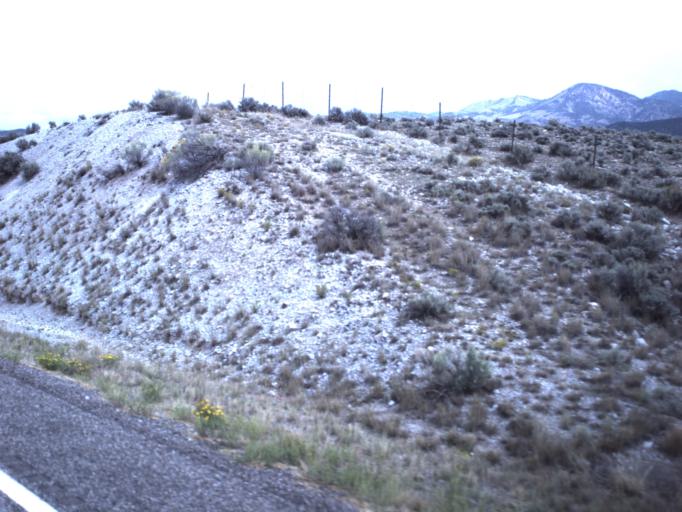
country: US
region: Utah
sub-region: Garfield County
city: Panguitch
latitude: 38.0104
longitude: -112.3754
